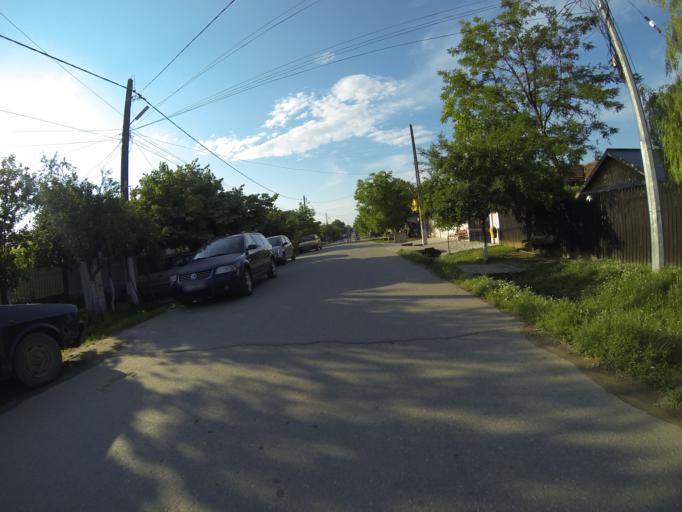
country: RO
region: Dolj
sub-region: Comuna Tuglui
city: Tuglui
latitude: 44.1788
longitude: 23.8155
